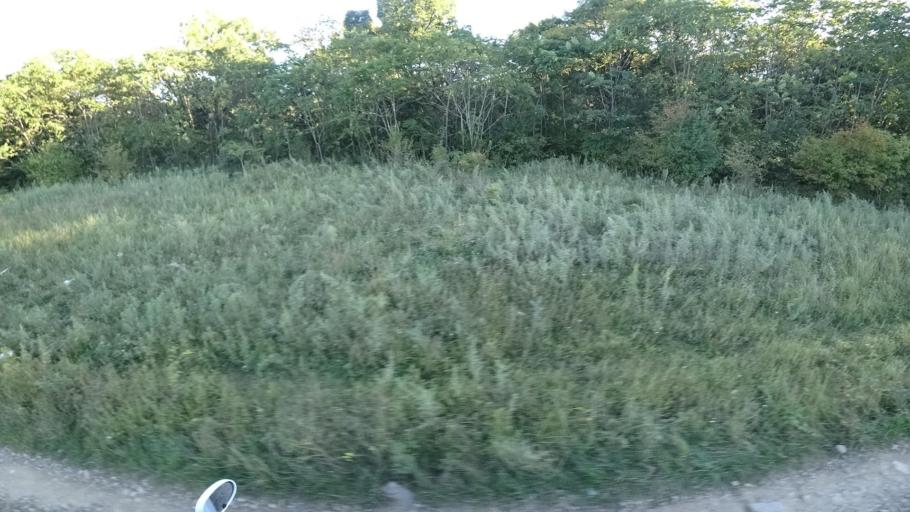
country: RU
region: Primorskiy
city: Kirovskiy
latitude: 44.8293
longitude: 133.5712
